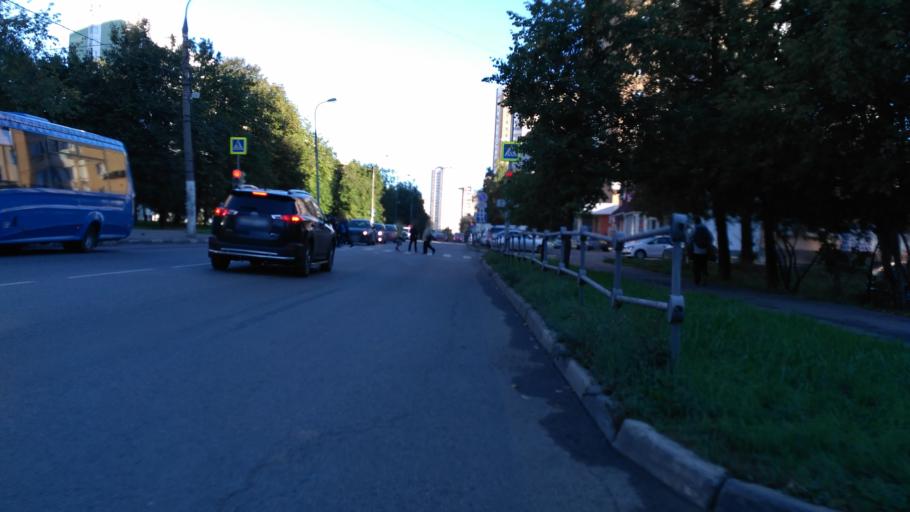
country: RU
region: Moskovskaya
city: Vostochnoe Degunino
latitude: 55.8673
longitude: 37.5581
